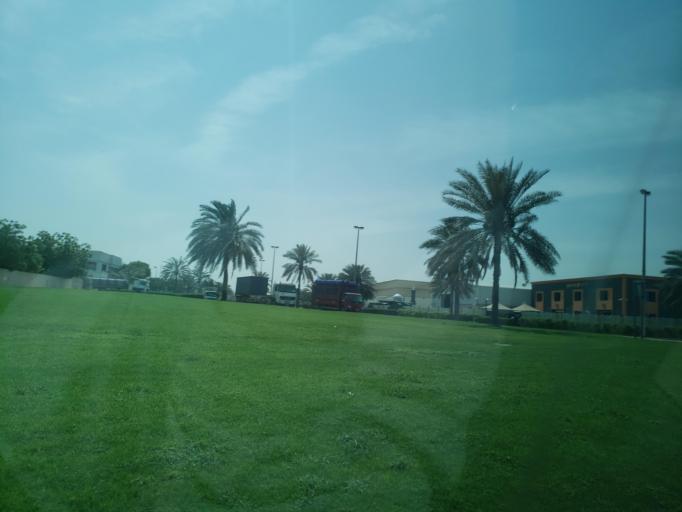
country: AE
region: Ash Shariqah
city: Sharjah
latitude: 25.3323
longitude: 55.4915
